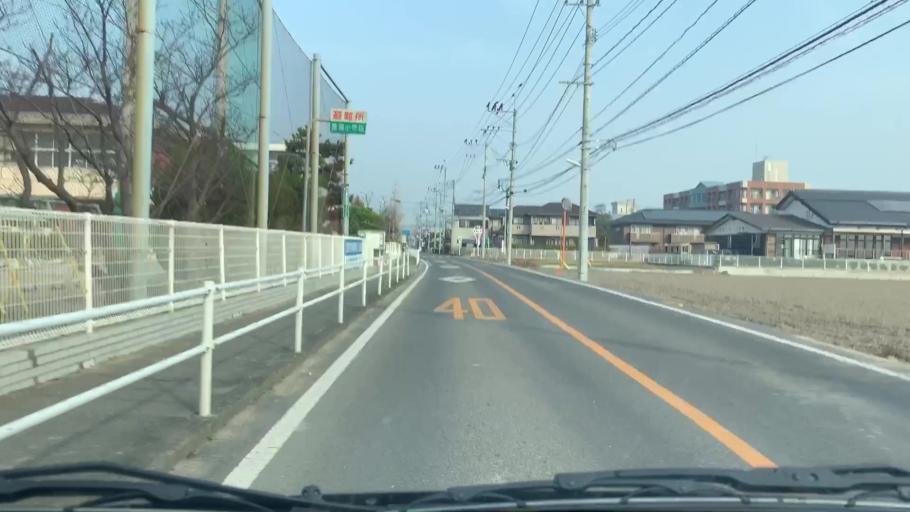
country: JP
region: Saga Prefecture
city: Saga-shi
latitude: 33.2403
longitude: 130.2584
